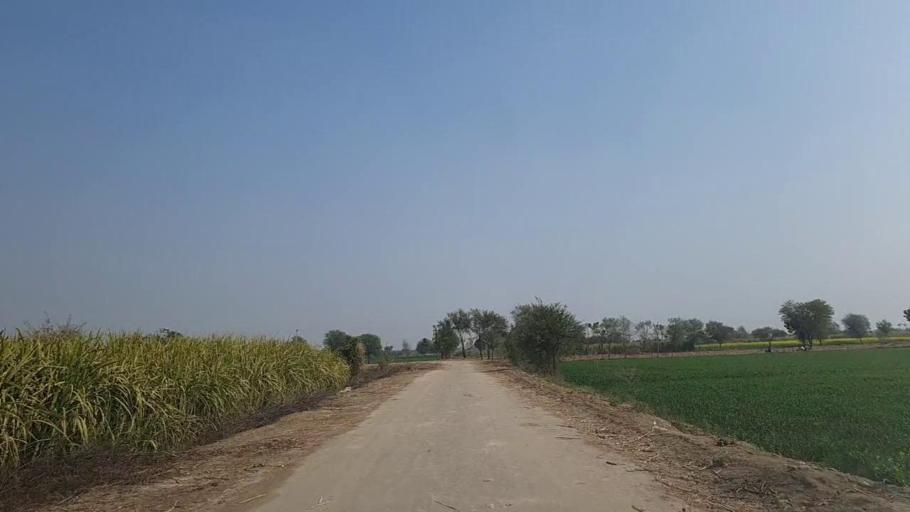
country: PK
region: Sindh
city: Daur
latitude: 26.4929
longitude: 68.4478
